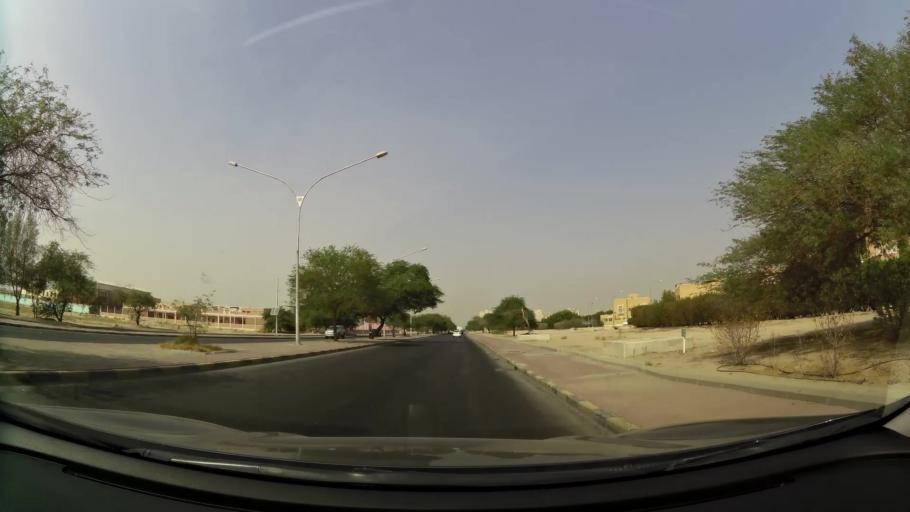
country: KW
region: Al Farwaniyah
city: Al Farwaniyah
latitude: 29.2470
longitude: 47.9339
